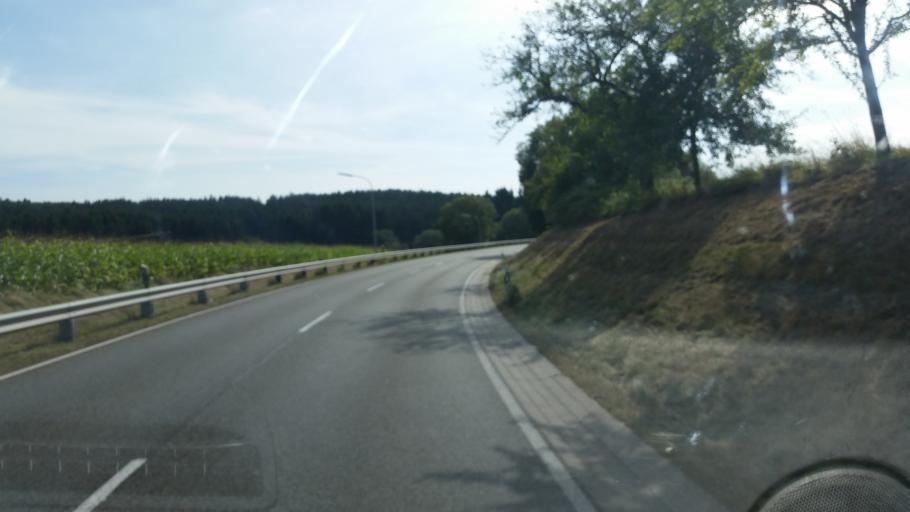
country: DE
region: Rheinland-Pfalz
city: Langenhahn
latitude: 50.5783
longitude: 7.9190
